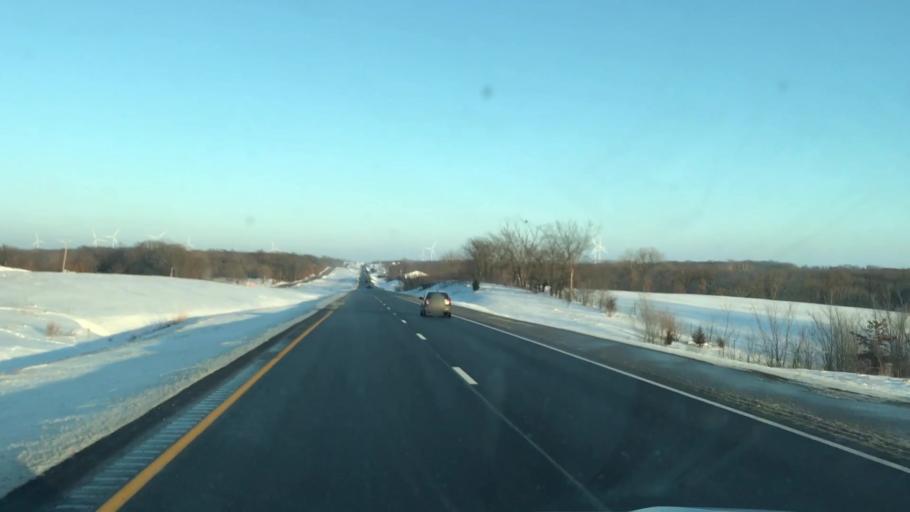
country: US
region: Missouri
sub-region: DeKalb County
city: Maysville
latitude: 39.7620
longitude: -94.4914
